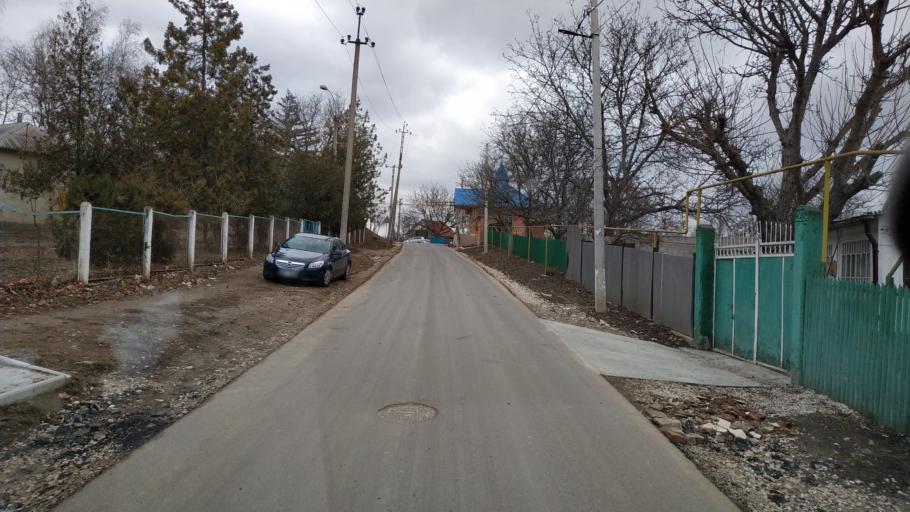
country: MD
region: Calarasi
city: Calarasi
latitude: 47.2392
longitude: 28.3104
